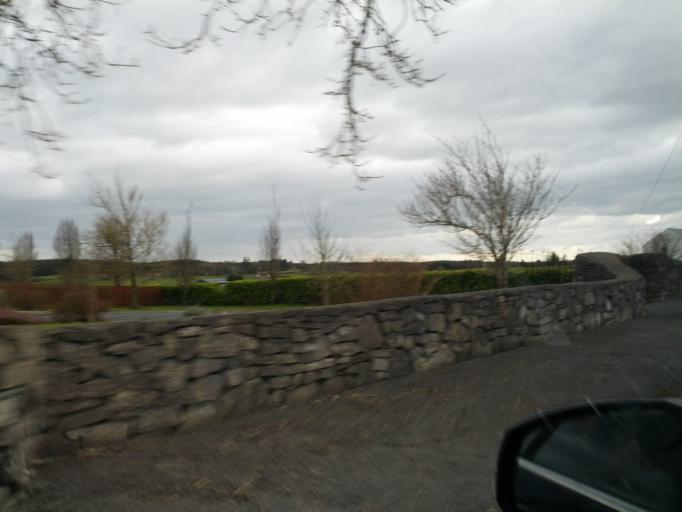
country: IE
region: Connaught
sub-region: County Galway
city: Athenry
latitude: 53.3933
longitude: -8.6423
